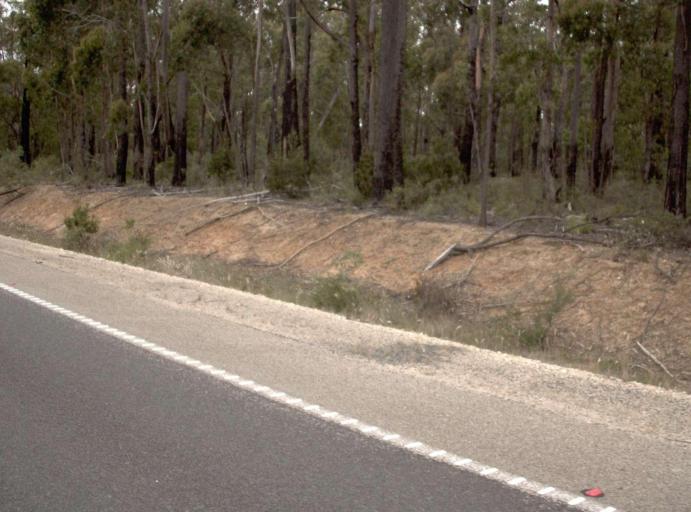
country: AU
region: Victoria
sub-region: East Gippsland
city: Lakes Entrance
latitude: -37.7119
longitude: 147.9830
